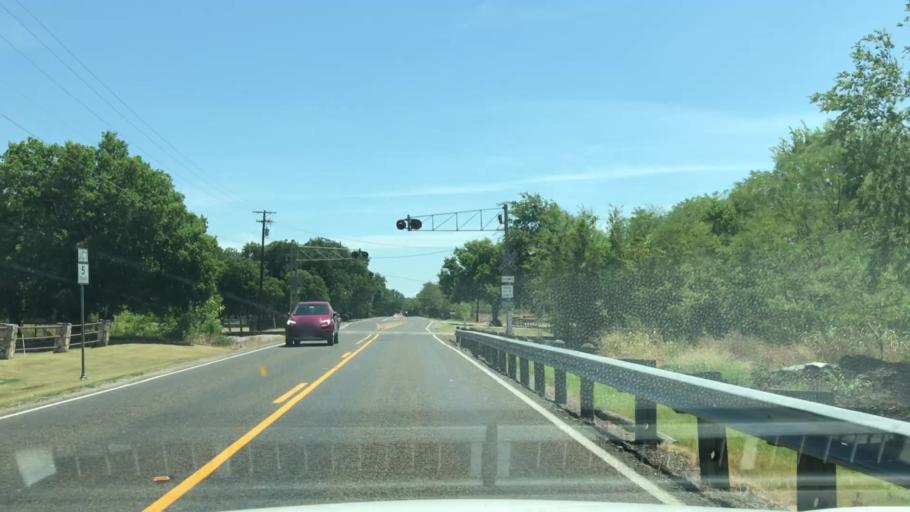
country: US
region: Texas
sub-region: Collin County
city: Fairview
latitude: 33.1565
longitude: -96.6272
